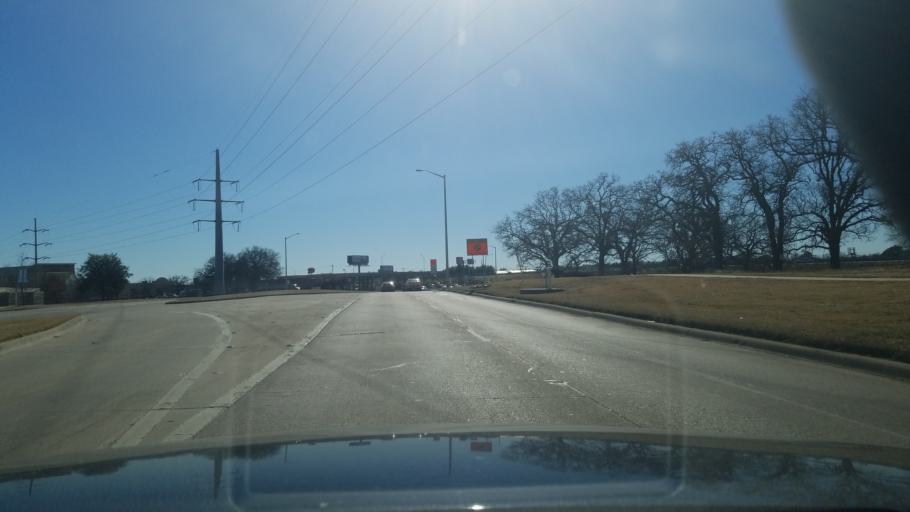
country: US
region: Texas
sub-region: Denton County
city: Corinth
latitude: 33.1763
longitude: -97.0885
